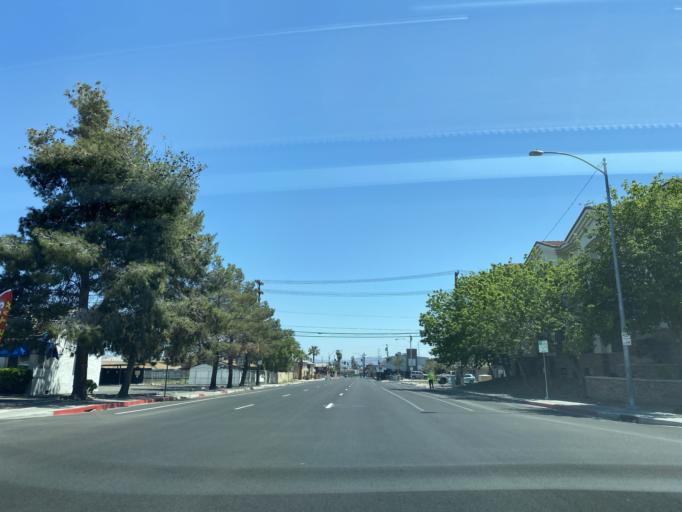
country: US
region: Nevada
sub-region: Clark County
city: Las Vegas
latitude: 36.1612
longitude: -115.1397
